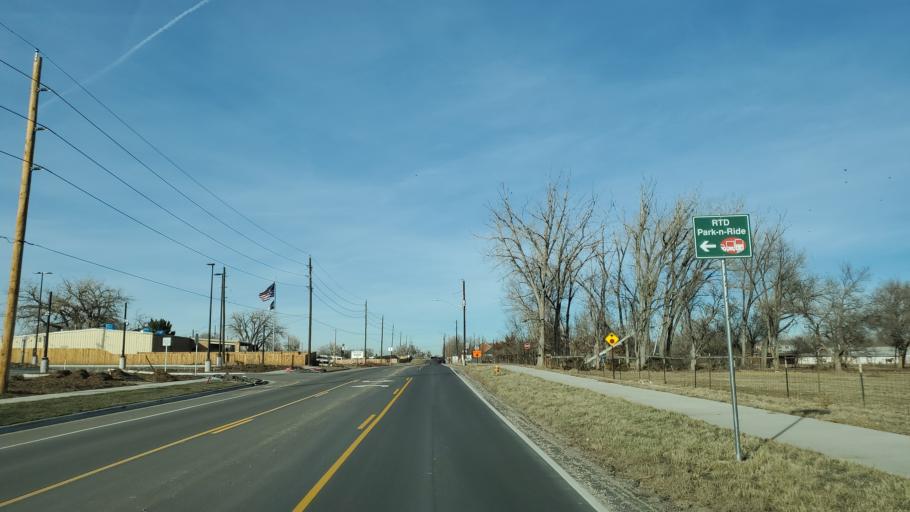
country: US
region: Colorado
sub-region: Adams County
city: Northglenn
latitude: 39.9025
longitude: -104.9589
